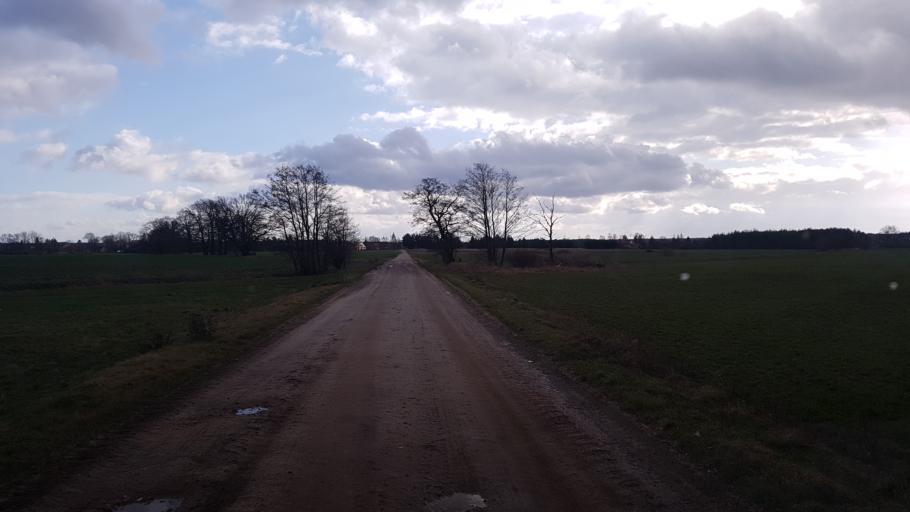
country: DE
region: Brandenburg
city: Sallgast
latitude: 51.6167
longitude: 13.8558
